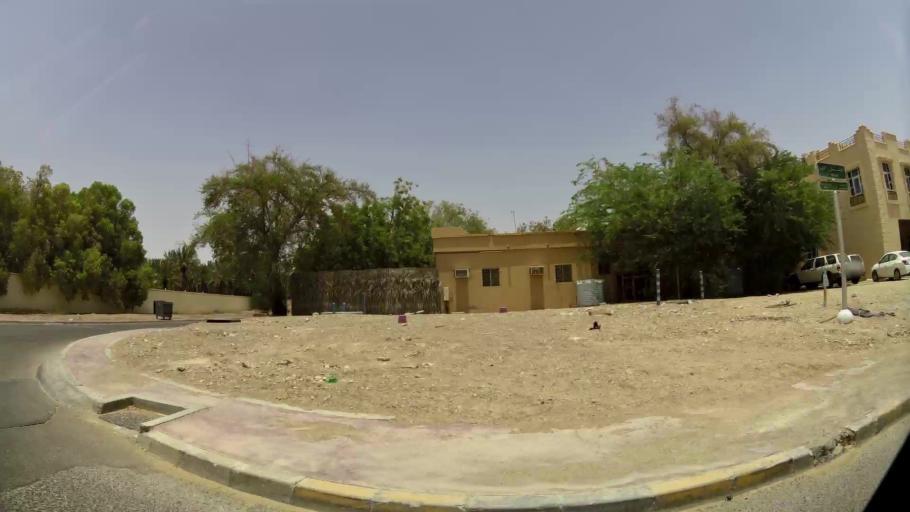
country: AE
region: Abu Dhabi
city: Al Ain
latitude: 24.2176
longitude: 55.7214
